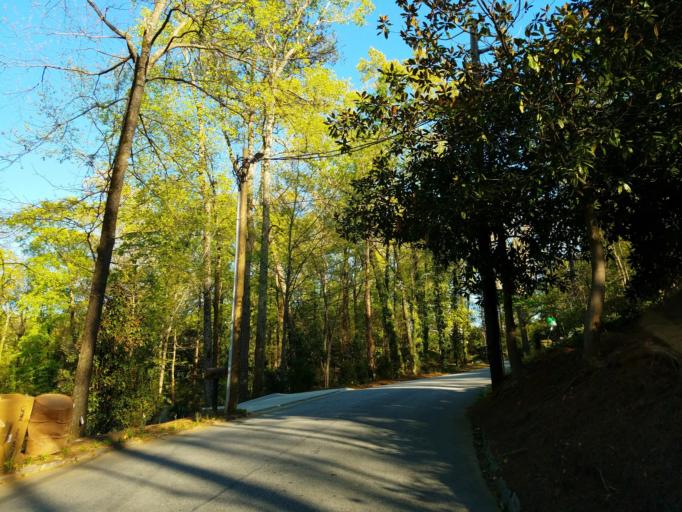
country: US
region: Georgia
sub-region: Cobb County
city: Vinings
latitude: 33.8474
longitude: -84.4525
